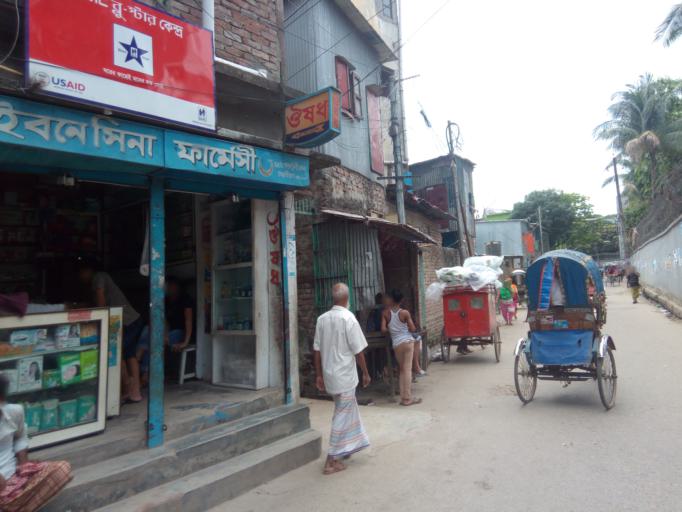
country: BD
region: Dhaka
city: Azimpur
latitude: 23.7286
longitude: 90.3759
